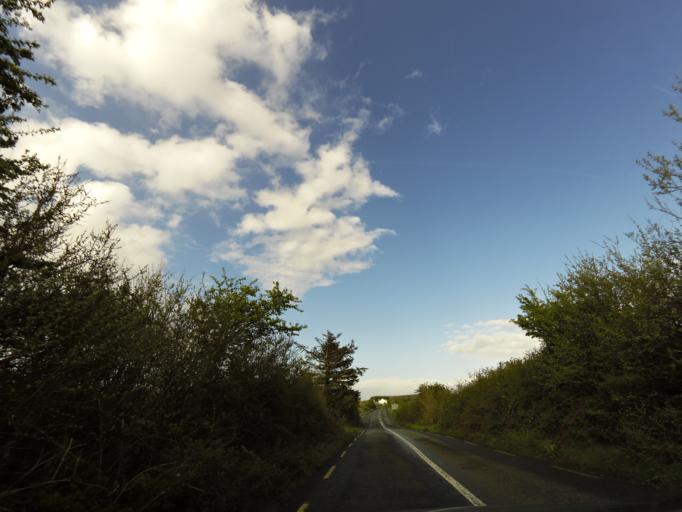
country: IE
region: Connaught
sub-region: County Galway
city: Bearna
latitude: 53.0194
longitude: -9.3137
